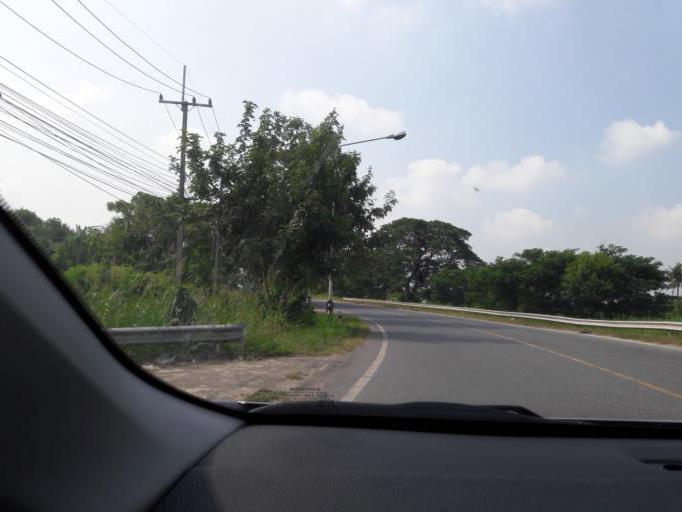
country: TH
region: Ang Thong
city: Ang Thong
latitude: 14.5883
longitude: 100.4439
